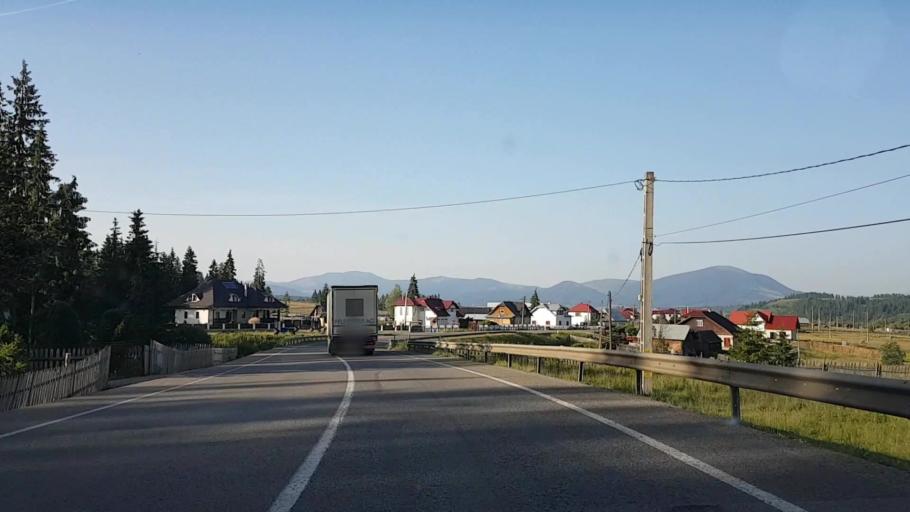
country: RO
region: Suceava
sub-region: Comuna Poiana Stampei
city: Poiana Stampei
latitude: 47.3068
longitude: 25.1223
